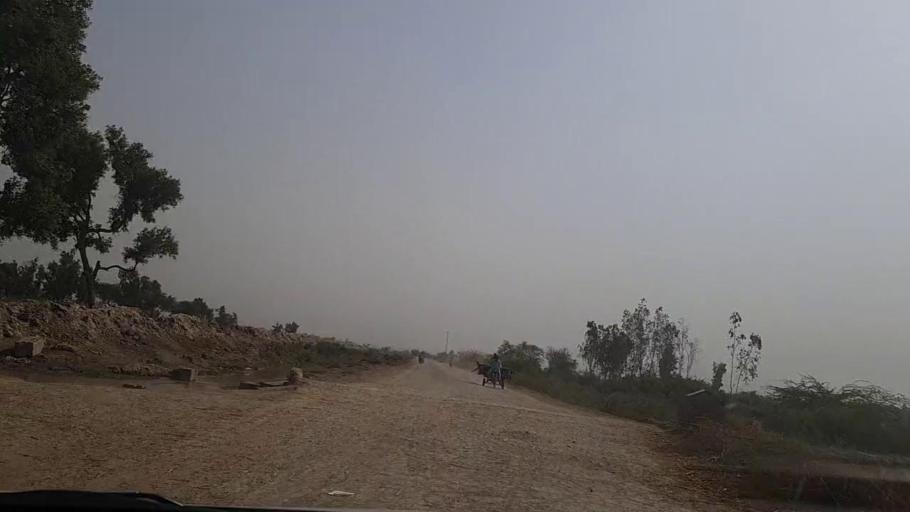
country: PK
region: Sindh
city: Pithoro
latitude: 25.4655
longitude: 69.2273
